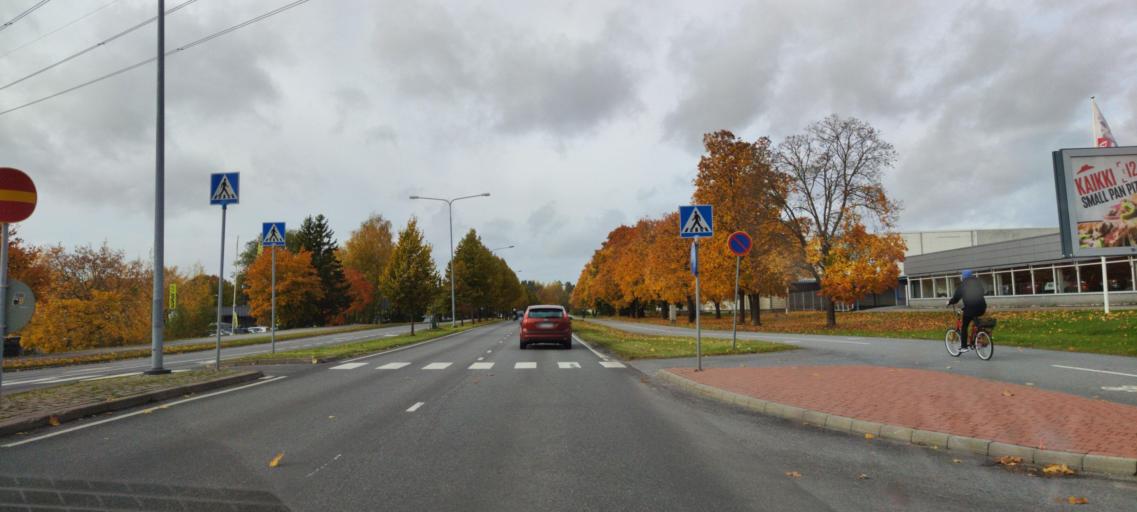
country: FI
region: Varsinais-Suomi
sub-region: Turku
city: Turku
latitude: 60.4679
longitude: 22.2442
